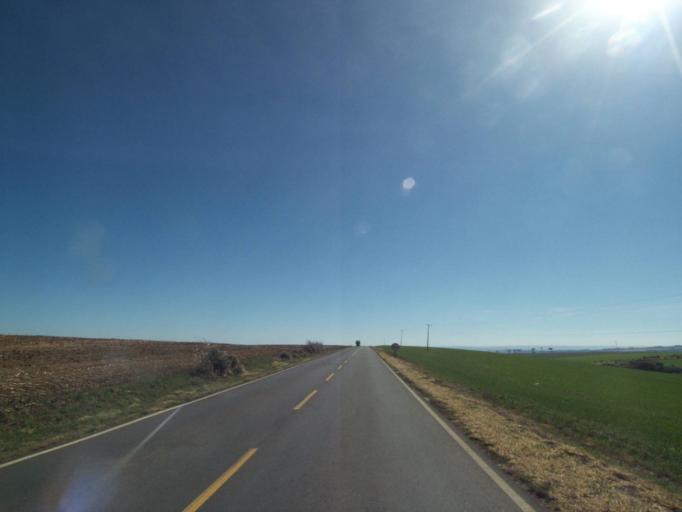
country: BR
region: Parana
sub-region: Tibagi
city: Tibagi
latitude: -24.5778
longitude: -50.2732
